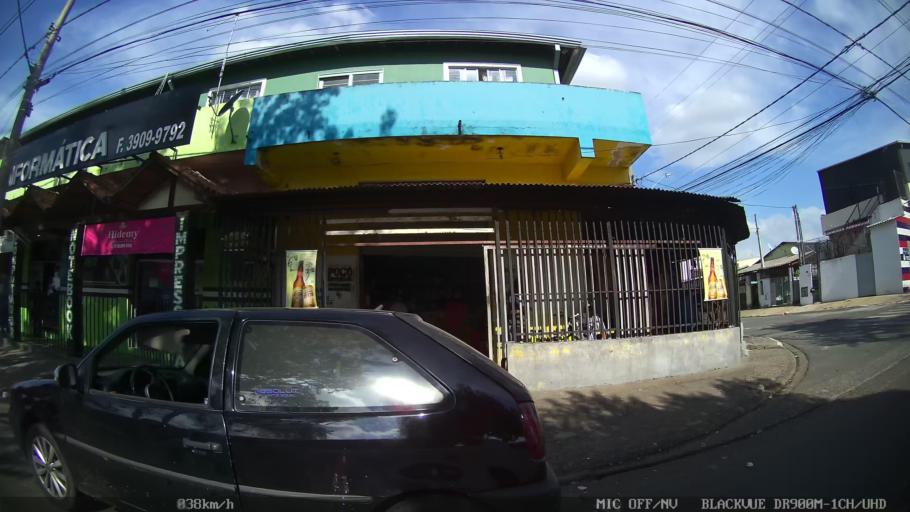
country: BR
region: Sao Paulo
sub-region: Hortolandia
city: Hortolandia
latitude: -22.8988
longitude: -47.2469
